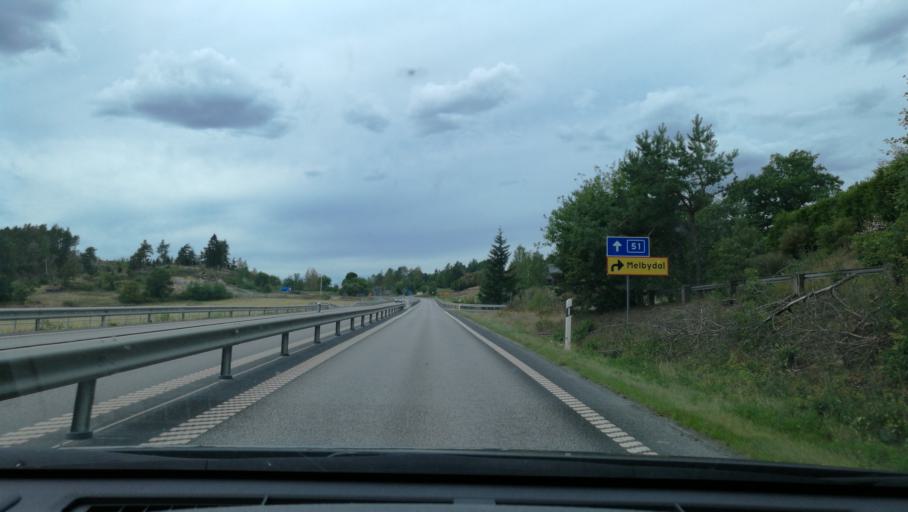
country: SE
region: OEstergoetland
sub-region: Norrkopings Kommun
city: Svartinge
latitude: 58.6827
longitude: 15.9390
